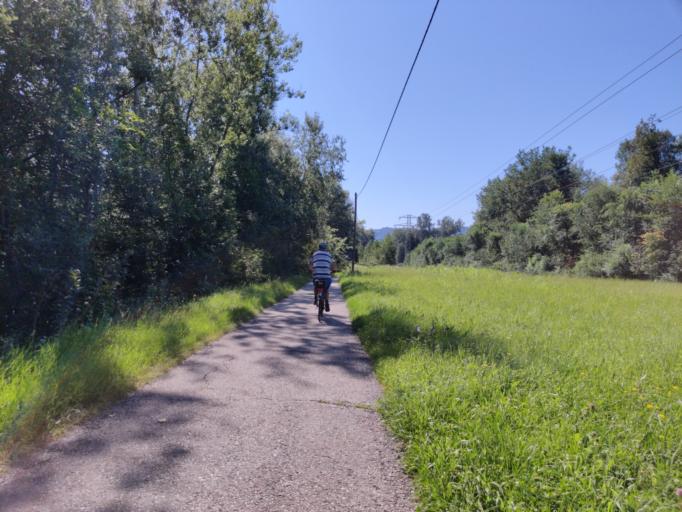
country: AT
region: Styria
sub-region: Politischer Bezirk Graz-Umgebung
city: Werndorf
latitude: 46.9027
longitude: 15.4921
